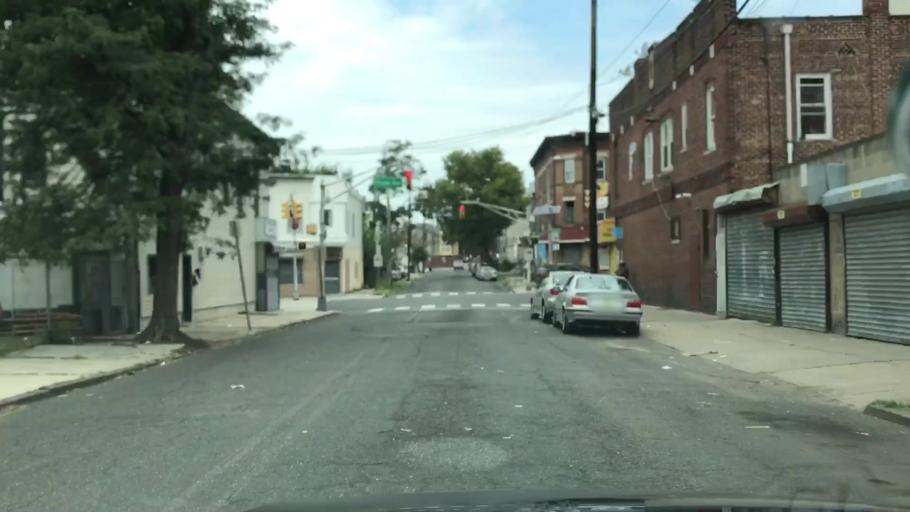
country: US
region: New Jersey
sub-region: Hudson County
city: Bayonne
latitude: 40.6917
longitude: -74.0945
